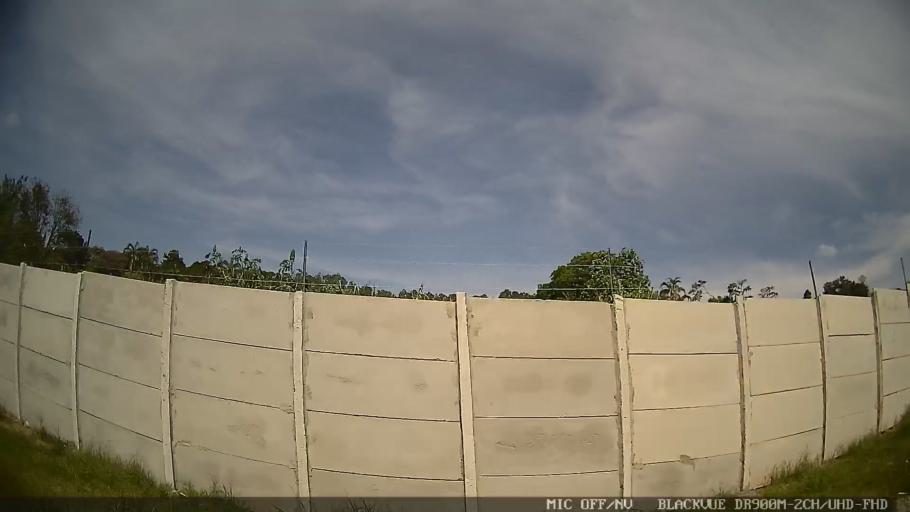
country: BR
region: Sao Paulo
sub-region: Itupeva
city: Itupeva
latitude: -23.2263
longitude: -47.0861
